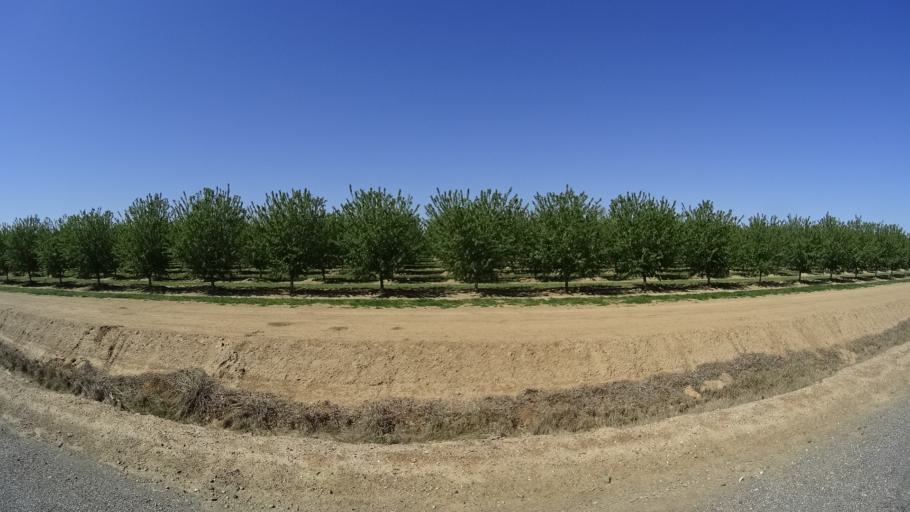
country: US
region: California
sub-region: Glenn County
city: Orland
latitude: 39.6948
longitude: -122.2340
